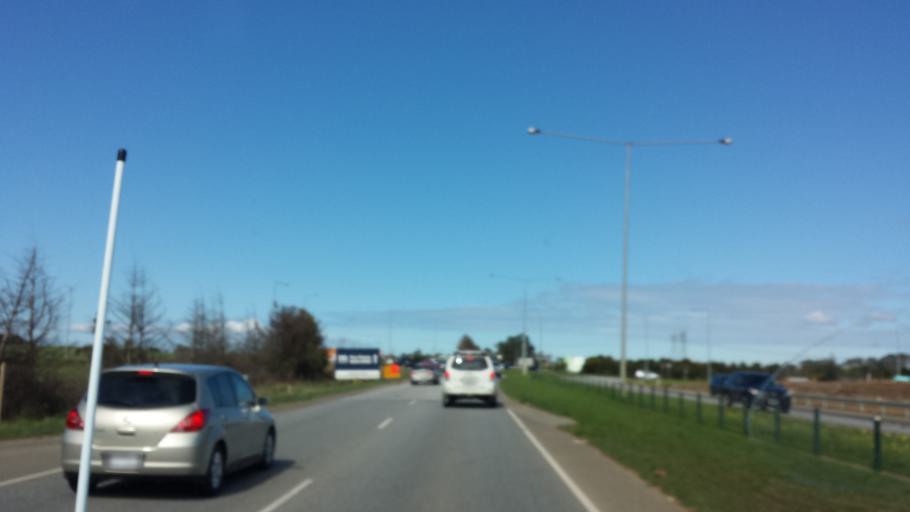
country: AU
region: Victoria
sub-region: Casey
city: Cranbourne East
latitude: -38.0878
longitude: 145.3332
